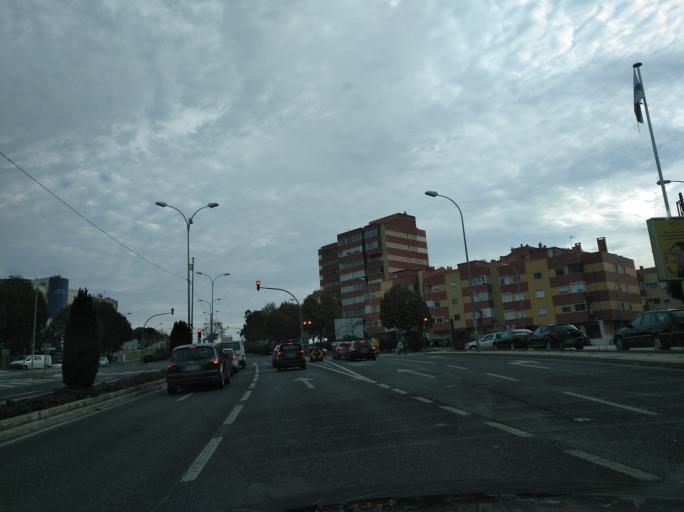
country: PT
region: Lisbon
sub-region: Amadora
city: Amadora
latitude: 38.7493
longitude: -9.2343
